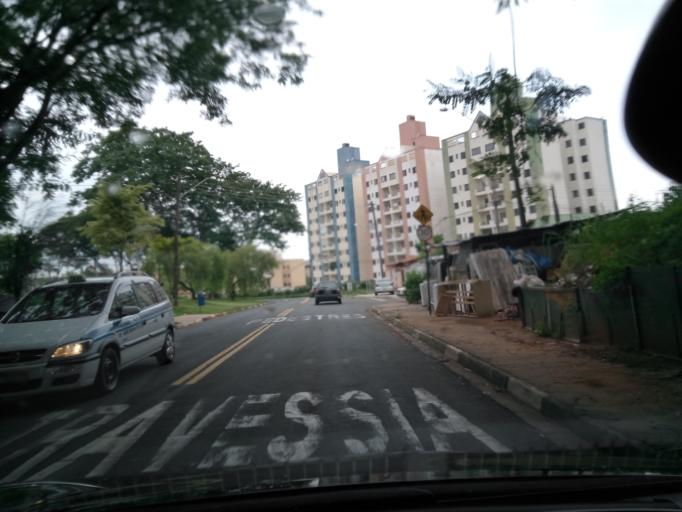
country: BR
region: Sao Paulo
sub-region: Campinas
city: Campinas
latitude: -22.8820
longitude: -47.0424
